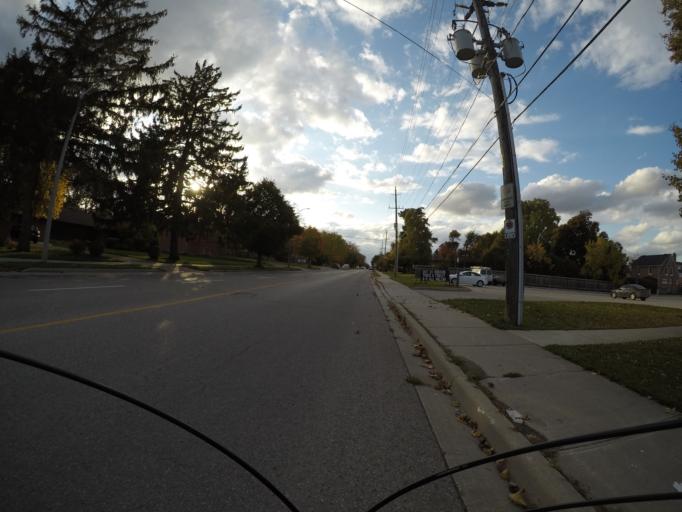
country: CA
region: Ontario
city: Waterloo
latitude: 43.5923
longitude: -80.5617
